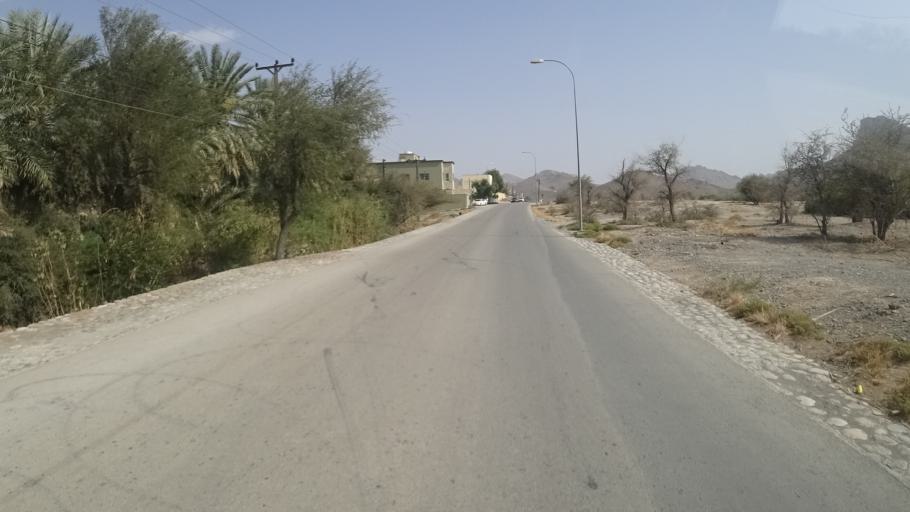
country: OM
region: Muhafazat ad Dakhiliyah
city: Bahla'
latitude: 23.0948
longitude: 57.3094
